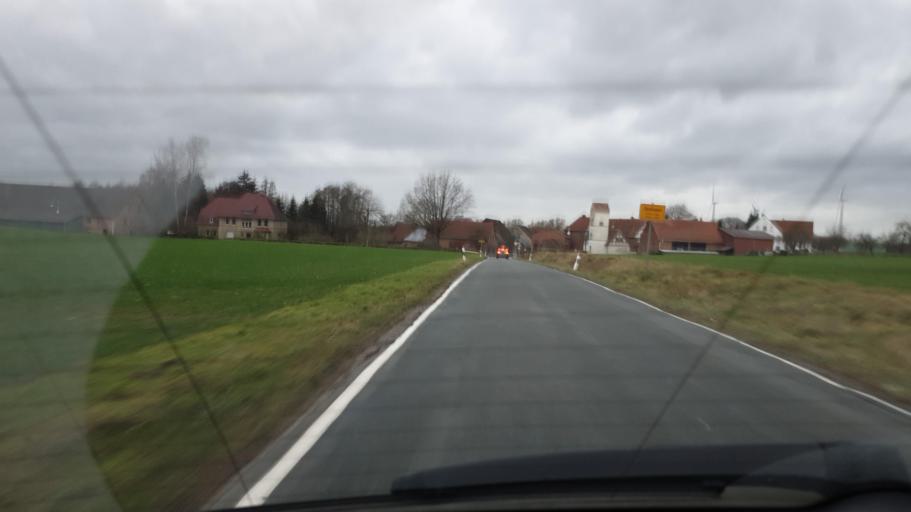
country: DE
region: North Rhine-Westphalia
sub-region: Regierungsbezirk Detmold
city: Lage
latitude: 52.0067
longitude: 8.8304
